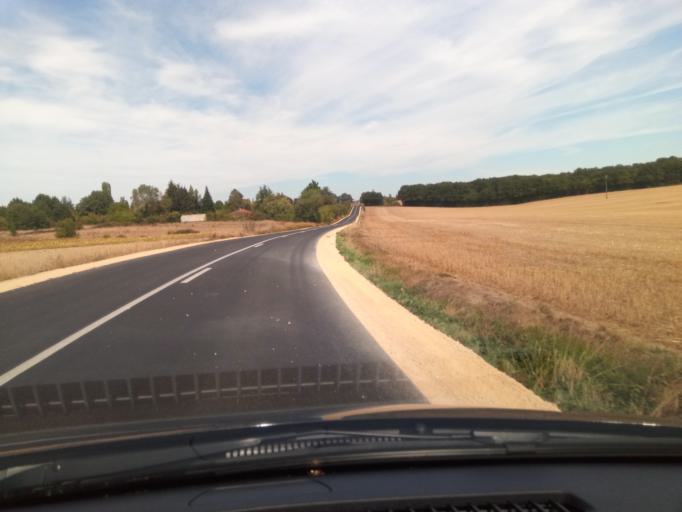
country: FR
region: Poitou-Charentes
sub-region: Departement de la Vienne
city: Terce
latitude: 46.5052
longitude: 0.5521
